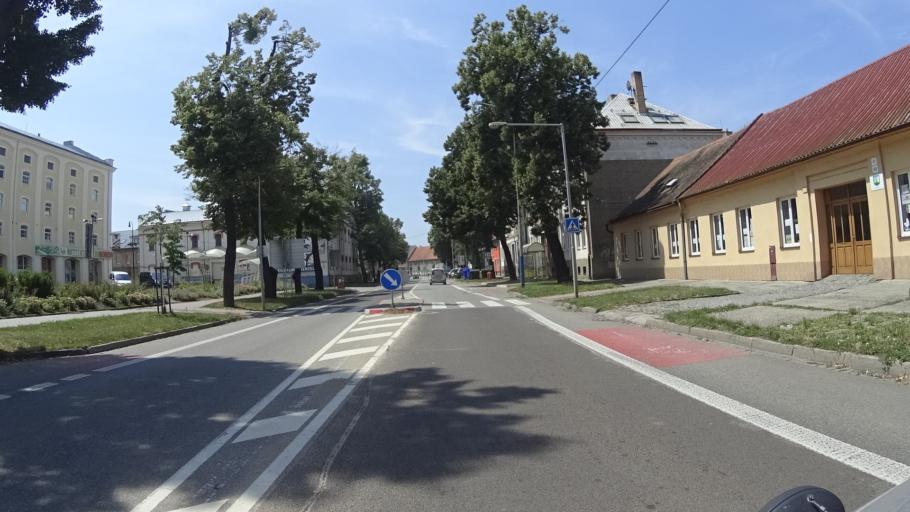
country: CZ
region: South Moravian
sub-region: Okres Breclav
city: Breclav
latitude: 48.7636
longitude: 16.8861
